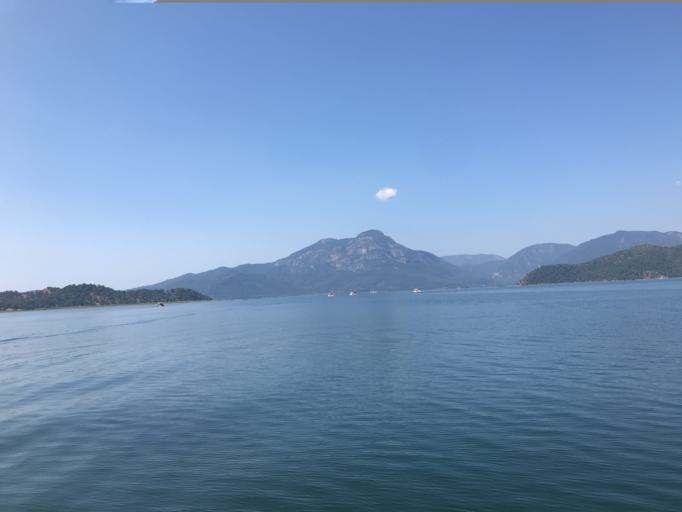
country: TR
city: Dalyan
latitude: 36.9134
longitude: 28.6554
